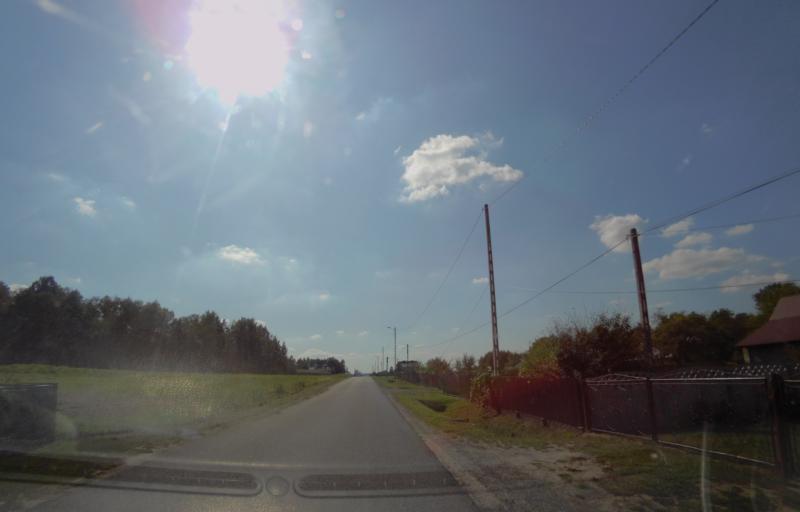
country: PL
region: Subcarpathian Voivodeship
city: Nowa Sarzyna
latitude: 50.2984
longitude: 22.3116
